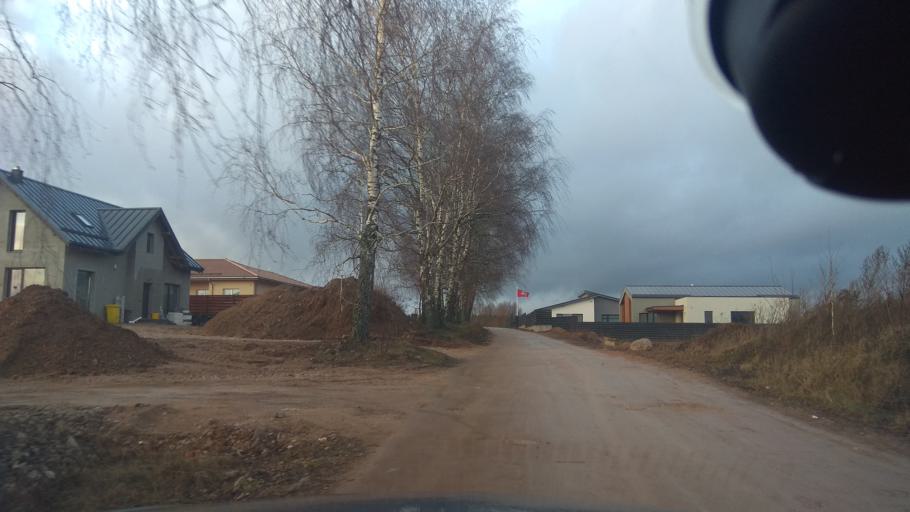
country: LT
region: Vilnius County
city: Pilaite
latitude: 54.7232
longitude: 25.1484
